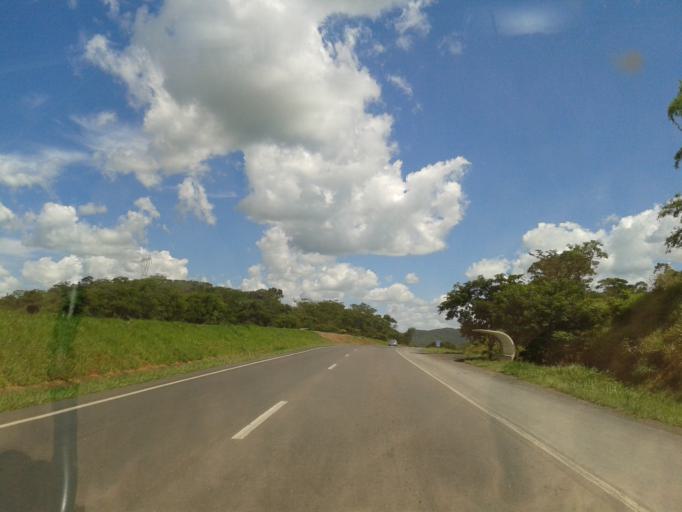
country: BR
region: Goias
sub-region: Piracanjuba
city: Piracanjuba
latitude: -17.3901
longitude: -49.2278
